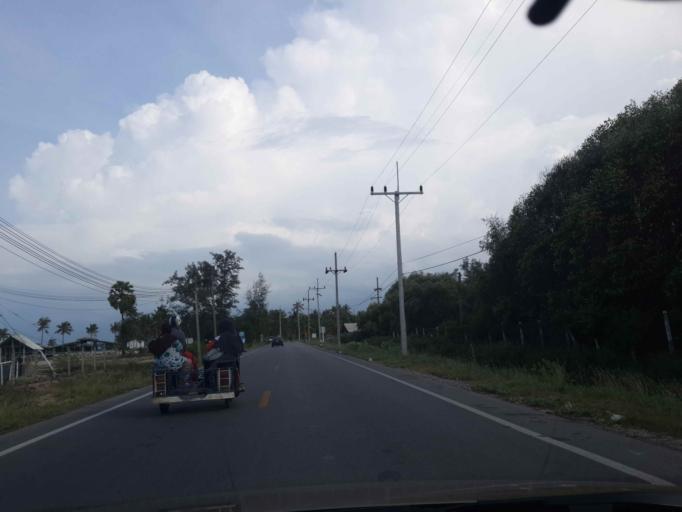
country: TH
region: Pattani
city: Yaring
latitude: 6.9198
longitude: 101.3324
